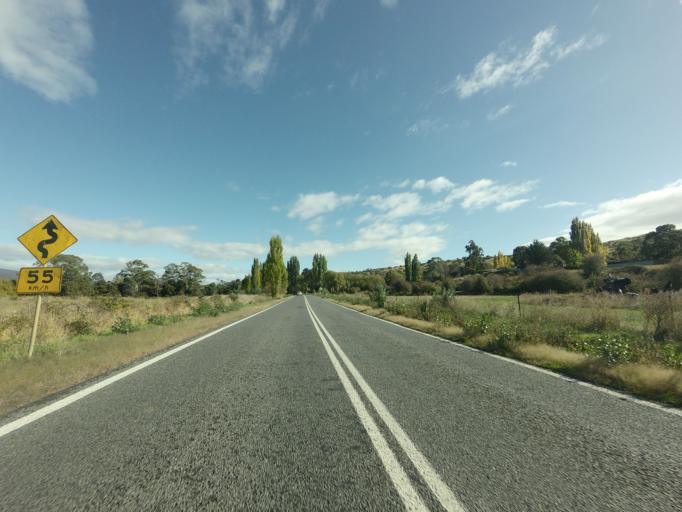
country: AU
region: Tasmania
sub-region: Derwent Valley
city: New Norfolk
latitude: -42.7608
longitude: 147.0112
